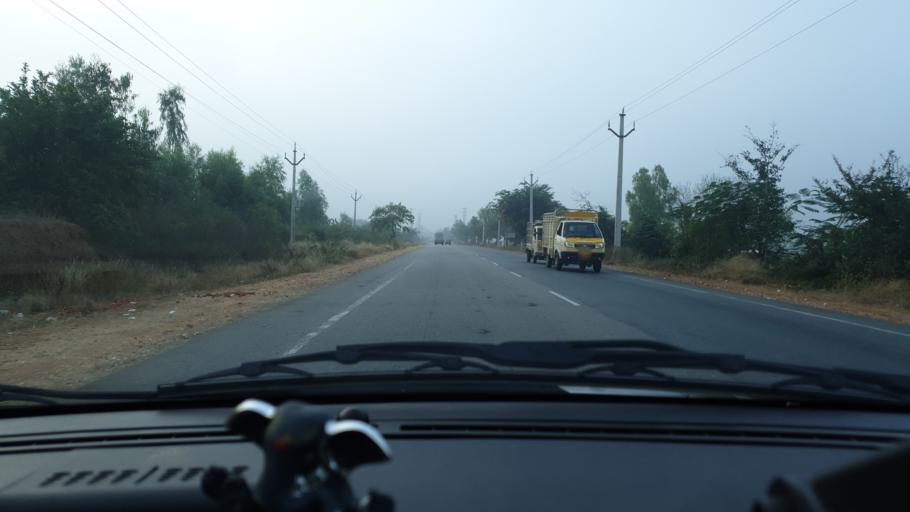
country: IN
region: Telangana
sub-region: Mahbubnagar
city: Farrukhnagar
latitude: 16.8904
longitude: 78.5297
